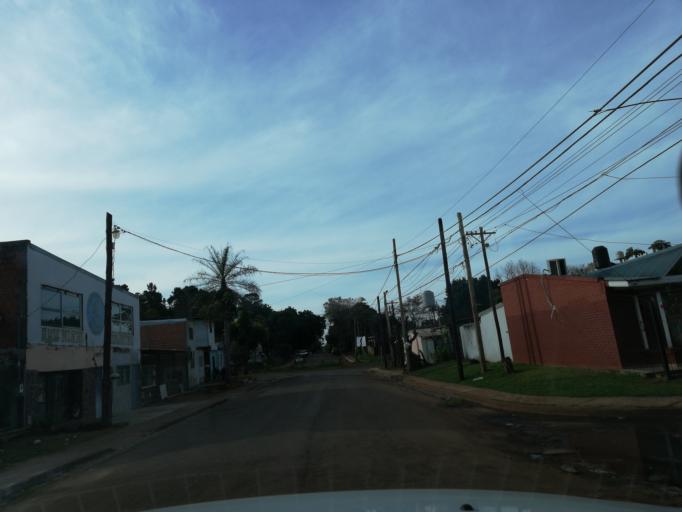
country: AR
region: Misiones
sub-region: Departamento de Capital
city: Posadas
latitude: -27.3843
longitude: -55.9360
